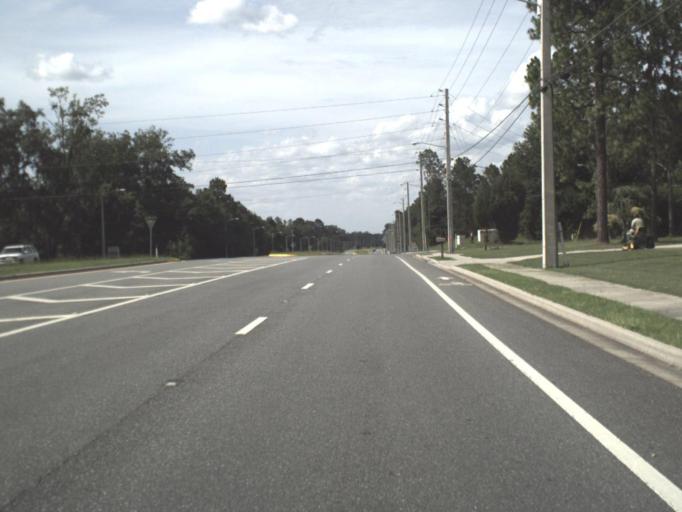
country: US
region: Florida
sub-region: Columbia County
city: Lake City
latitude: 30.1258
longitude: -82.6529
